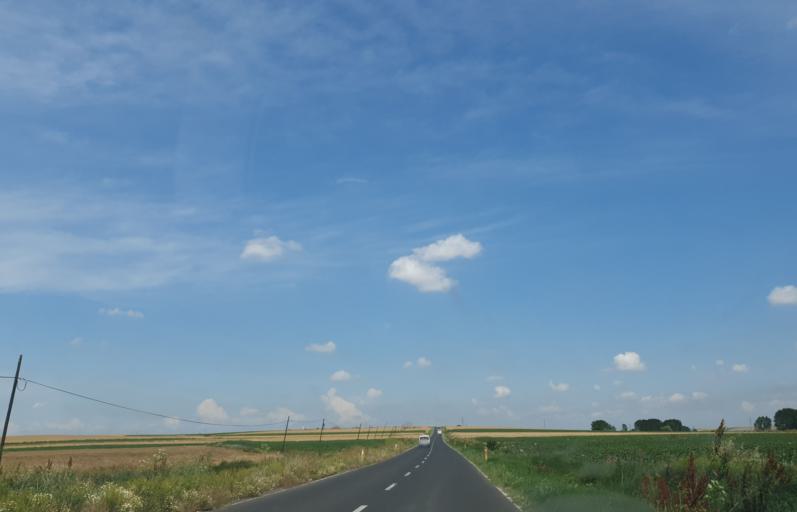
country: TR
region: Kirklareli
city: Buyukkaristiran
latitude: 41.2265
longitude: 27.5620
